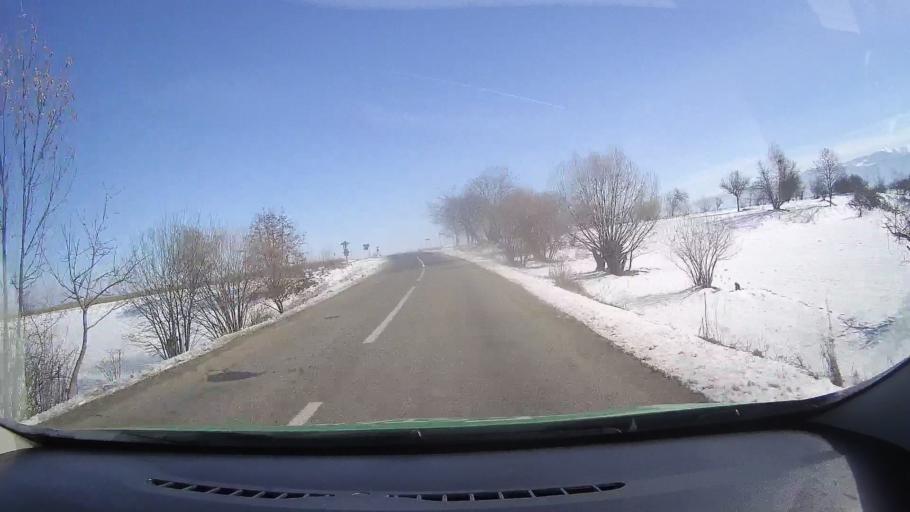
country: RO
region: Brasov
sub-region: Comuna Lisa
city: Lisa
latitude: 45.7260
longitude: 24.8756
